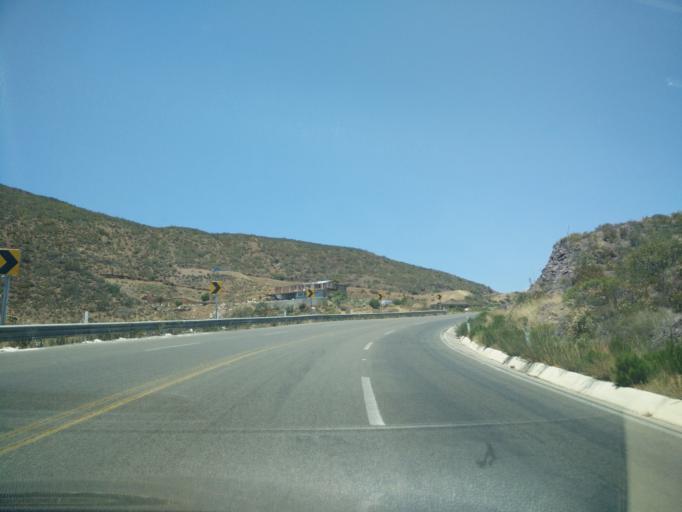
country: MX
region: Baja California
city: El Sauzal
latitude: 31.9346
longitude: -116.6705
